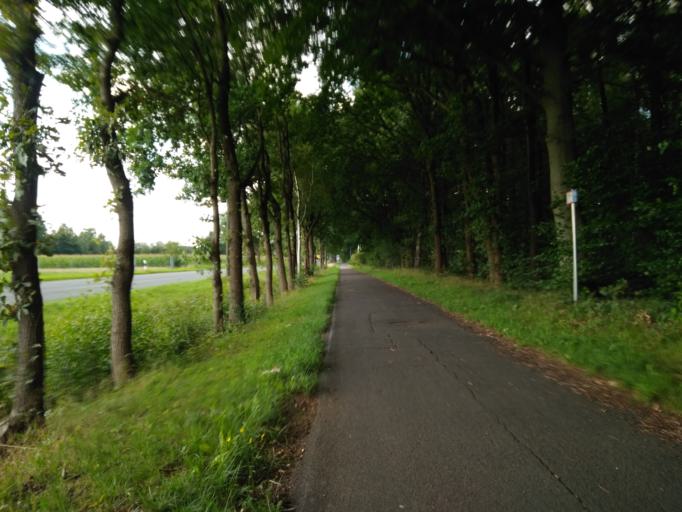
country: DE
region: North Rhine-Westphalia
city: Dorsten
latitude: 51.7014
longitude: 6.9718
